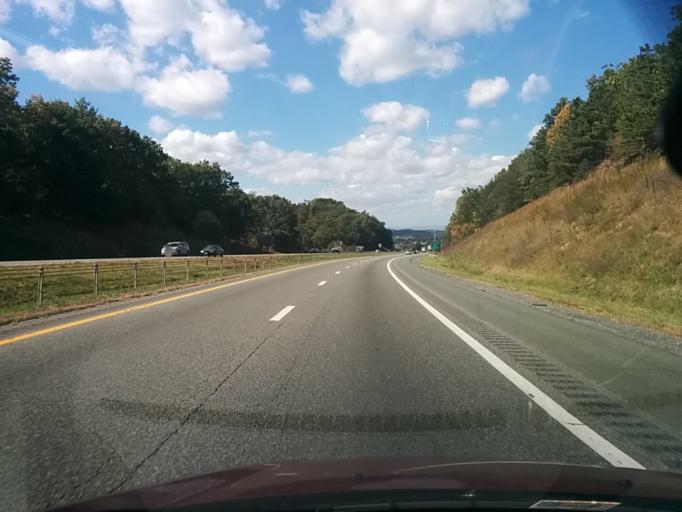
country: US
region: Virginia
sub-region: City of Waynesboro
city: Waynesboro
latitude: 38.0403
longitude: -78.8954
